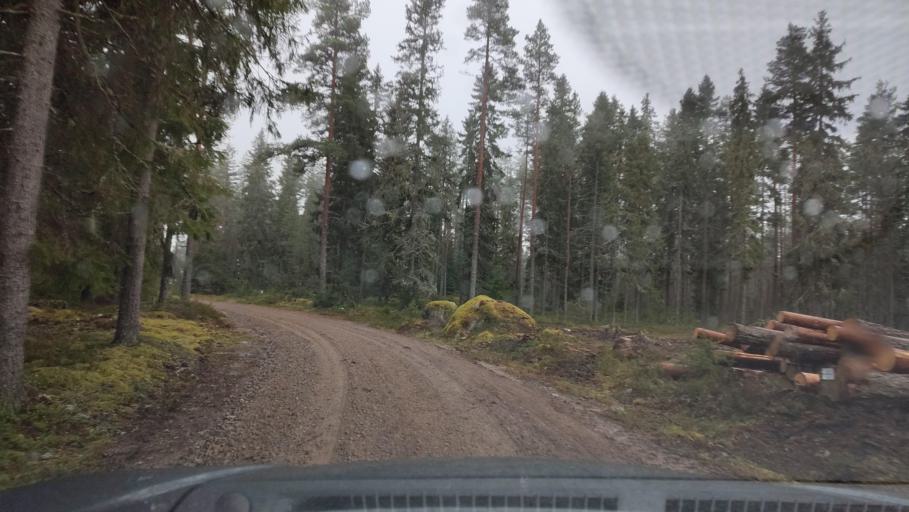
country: FI
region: Southern Ostrobothnia
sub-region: Suupohja
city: Karijoki
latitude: 62.1977
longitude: 21.7811
